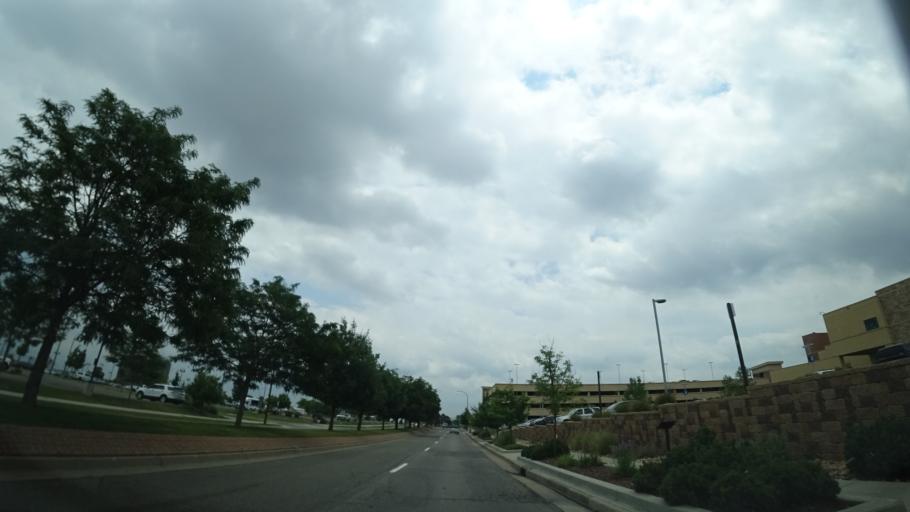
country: US
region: Colorado
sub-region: Jefferson County
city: Lakewood
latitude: 39.7180
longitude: -105.1300
